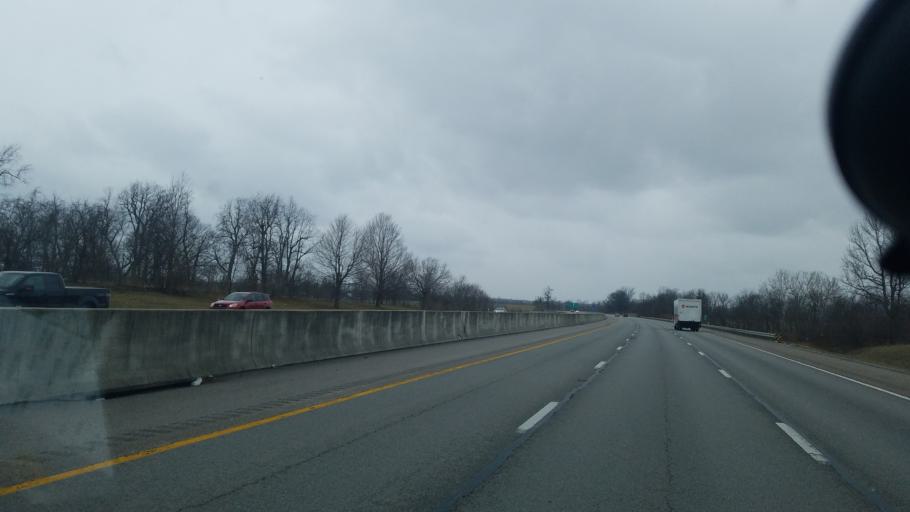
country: US
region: Kentucky
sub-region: Fayette County
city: Lexington-Fayette
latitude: 38.0613
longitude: -84.3808
